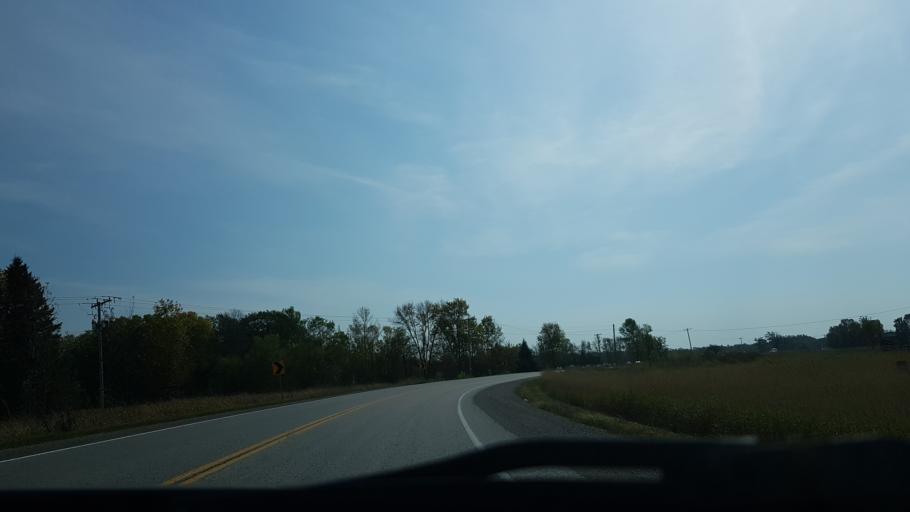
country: CA
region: Ontario
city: Orillia
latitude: 44.6503
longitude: -79.1190
